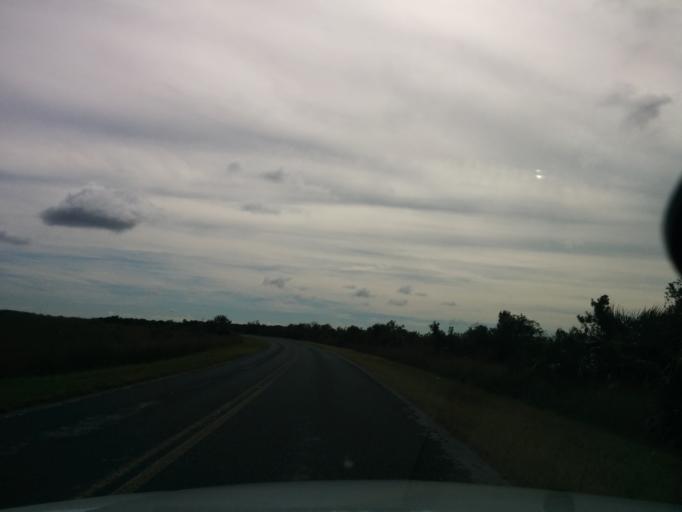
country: US
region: Florida
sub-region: Miami-Dade County
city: Florida City
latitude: 25.3920
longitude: -80.6170
